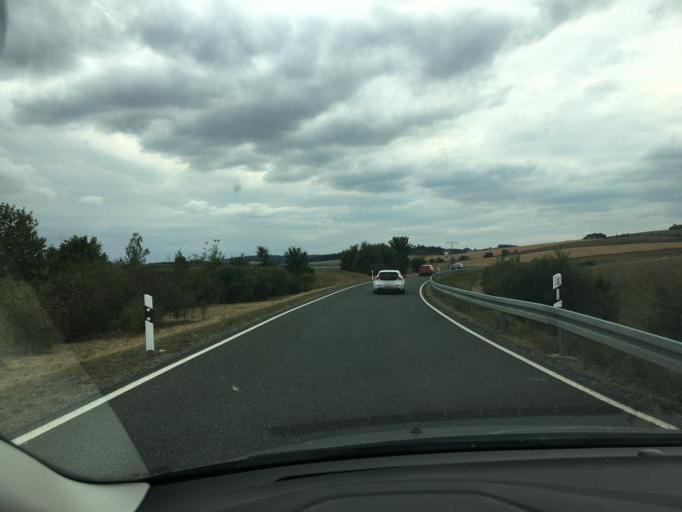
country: DE
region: Thuringia
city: Bad Lobenstein
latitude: 50.4550
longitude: 11.6621
